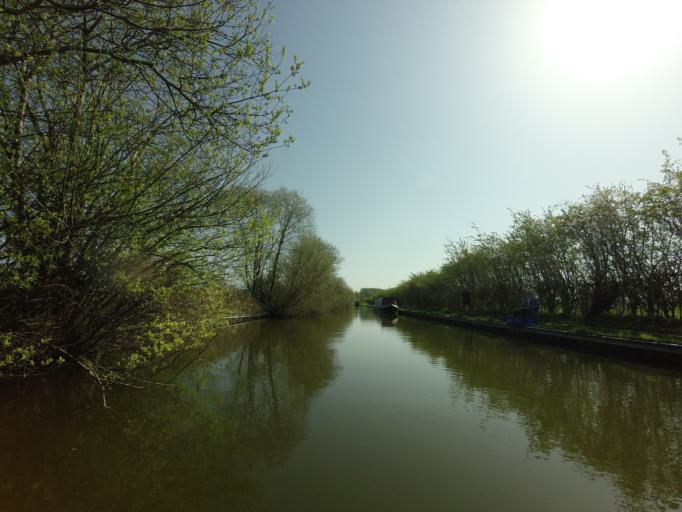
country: GB
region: England
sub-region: Buckinghamshire
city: Cheddington
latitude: 51.8216
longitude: -0.6811
